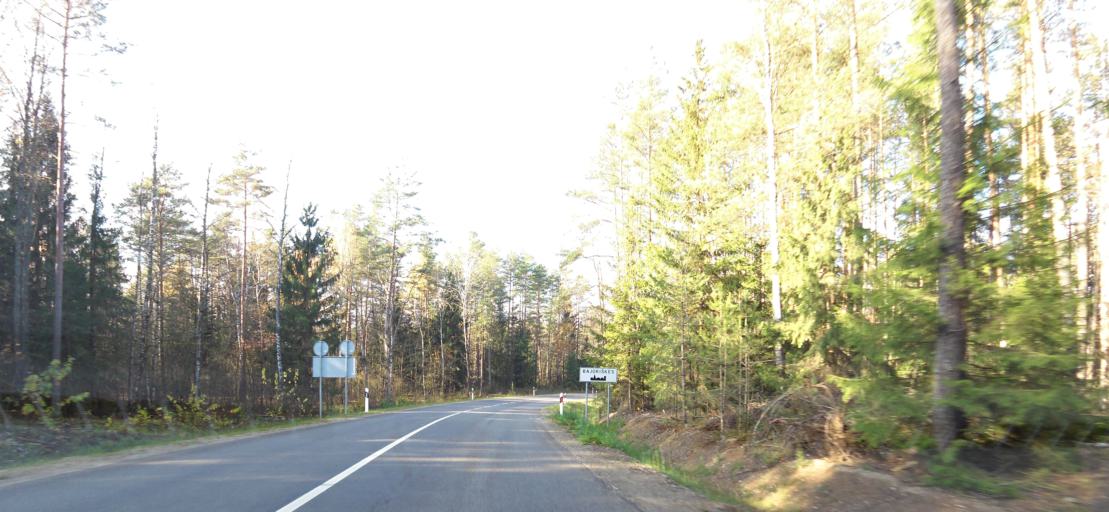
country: LT
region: Vilnius County
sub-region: Trakai
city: Rudiskes
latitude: 54.5090
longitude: 24.8834
